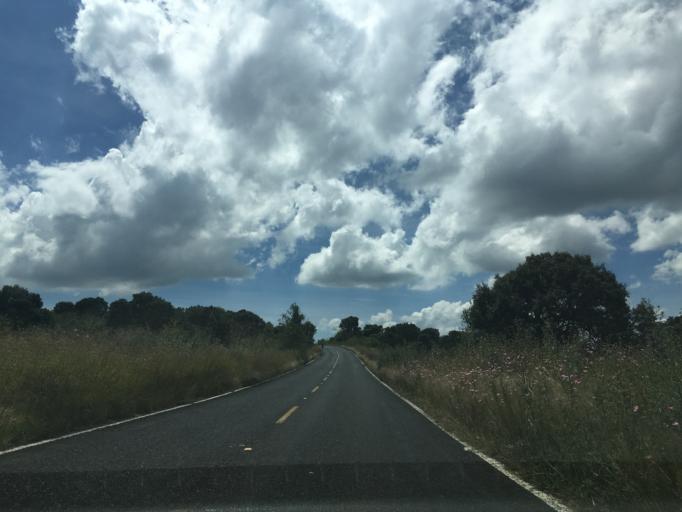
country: MX
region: Michoacan
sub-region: Morelia
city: Cuto de la Esperanza
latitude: 19.7538
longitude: -101.3711
